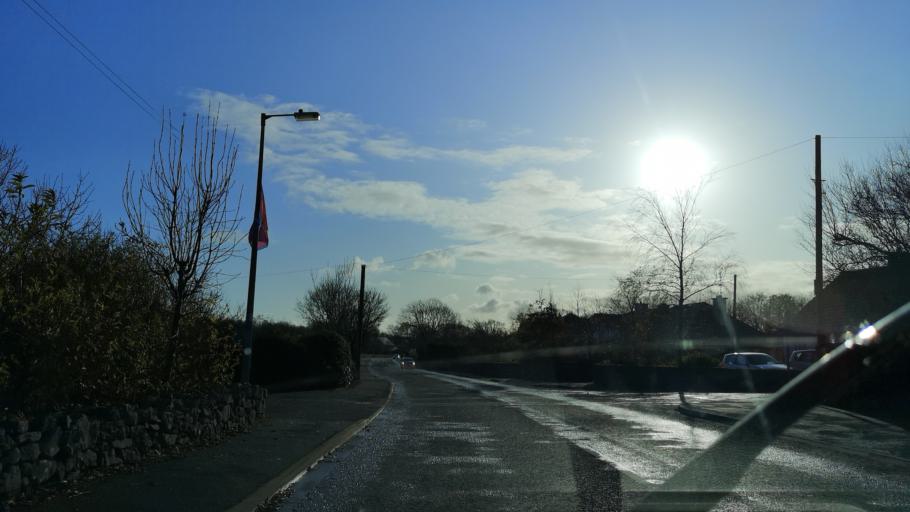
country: IE
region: Connaught
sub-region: County Galway
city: Oranmore
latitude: 53.2620
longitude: -8.9328
